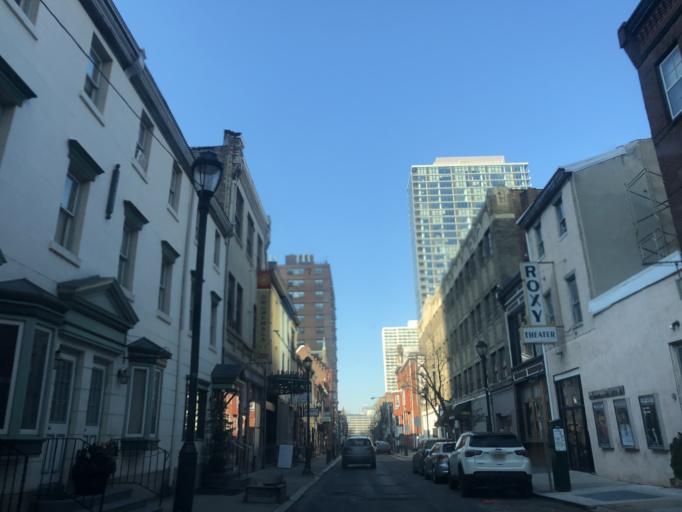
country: US
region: Pennsylvania
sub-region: Philadelphia County
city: Philadelphia
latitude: 39.9514
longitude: -75.1742
